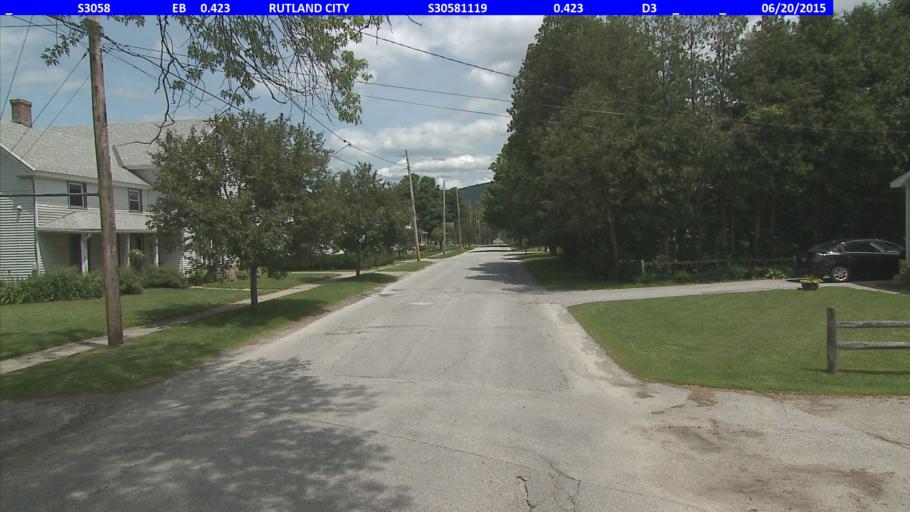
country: US
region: Vermont
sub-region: Rutland County
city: Rutland
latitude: 43.6153
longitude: -72.9653
